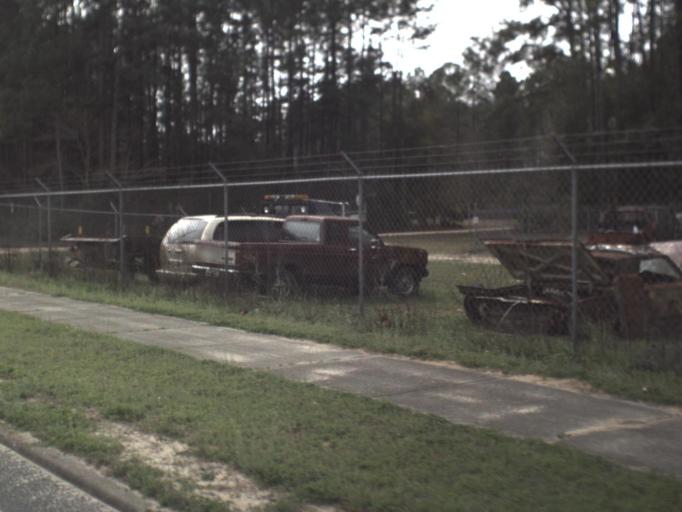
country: US
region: Florida
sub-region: Bay County
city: Youngstown
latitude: 30.4815
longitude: -85.4198
